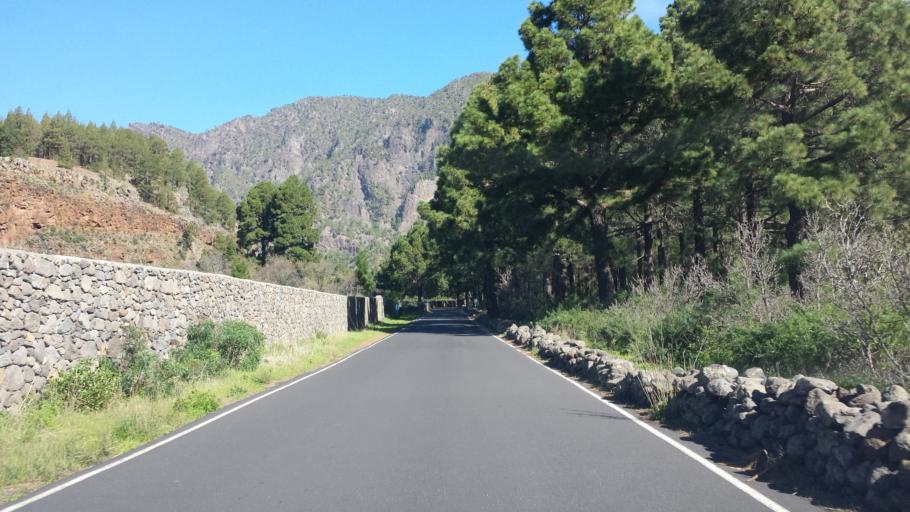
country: ES
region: Canary Islands
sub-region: Provincia de Santa Cruz de Tenerife
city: El Paso
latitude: 28.6686
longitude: -17.8478
